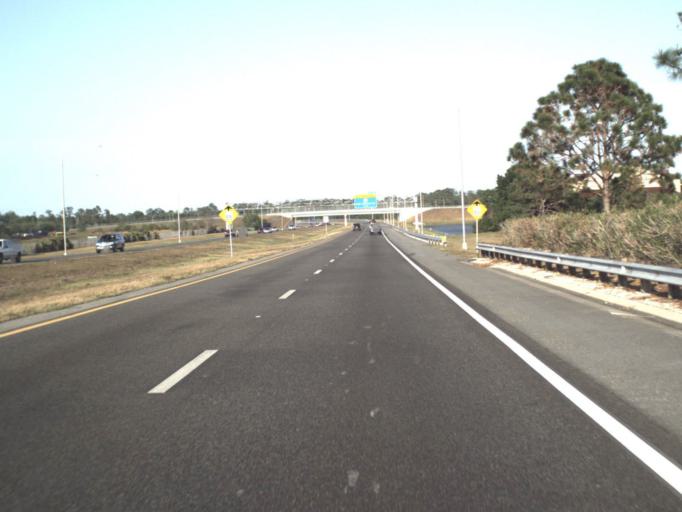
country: US
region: Florida
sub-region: Orange County
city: Alafaya
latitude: 28.5506
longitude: -81.2002
